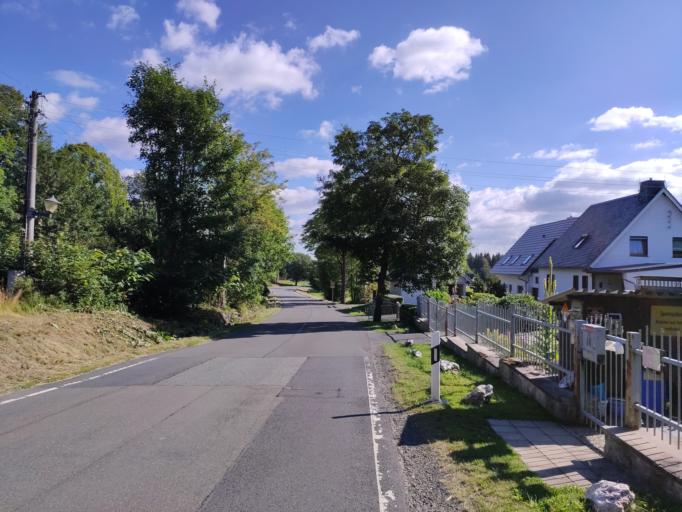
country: DE
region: Thuringia
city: Wurzbach
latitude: 50.4192
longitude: 11.5305
